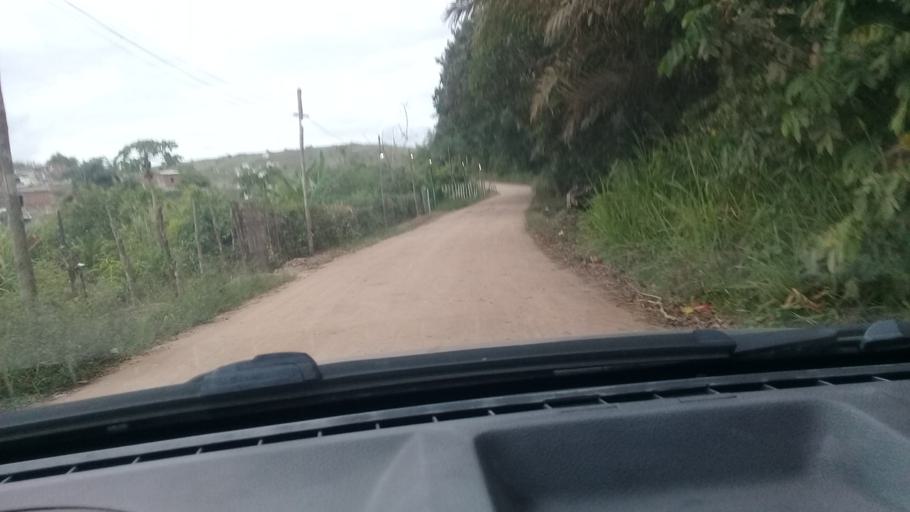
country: BR
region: Pernambuco
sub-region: Jaboatao Dos Guararapes
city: Jaboatao dos Guararapes
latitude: -8.0836
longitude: -35.0338
